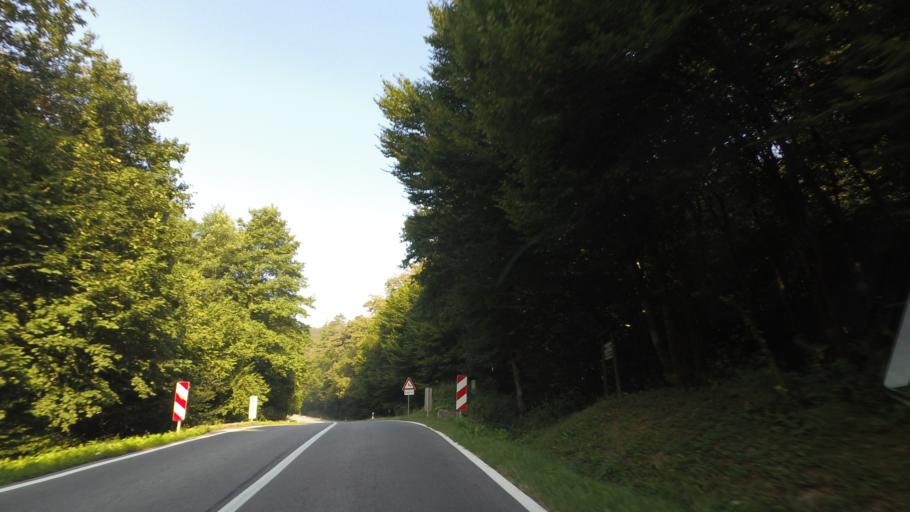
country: HR
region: Brodsko-Posavska
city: Cernik
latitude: 45.4570
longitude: 17.4565
